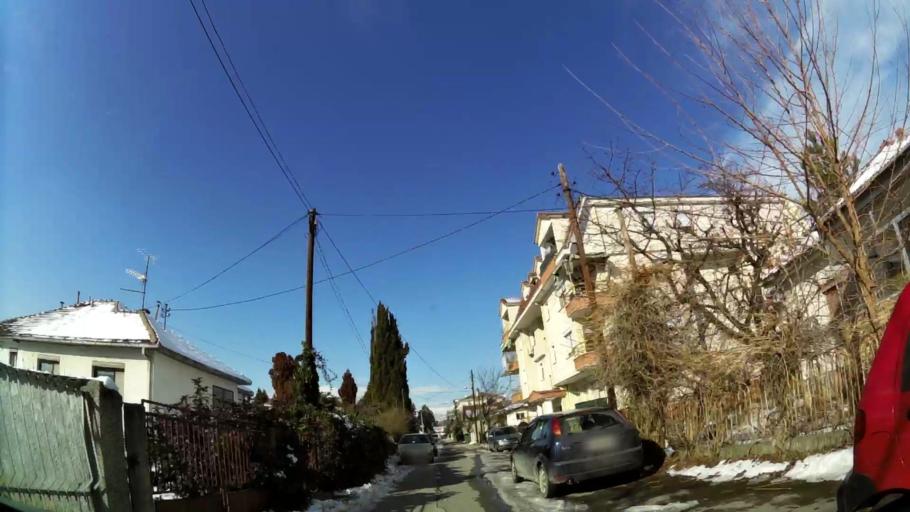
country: MK
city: Krushopek
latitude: 42.0052
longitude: 21.3691
